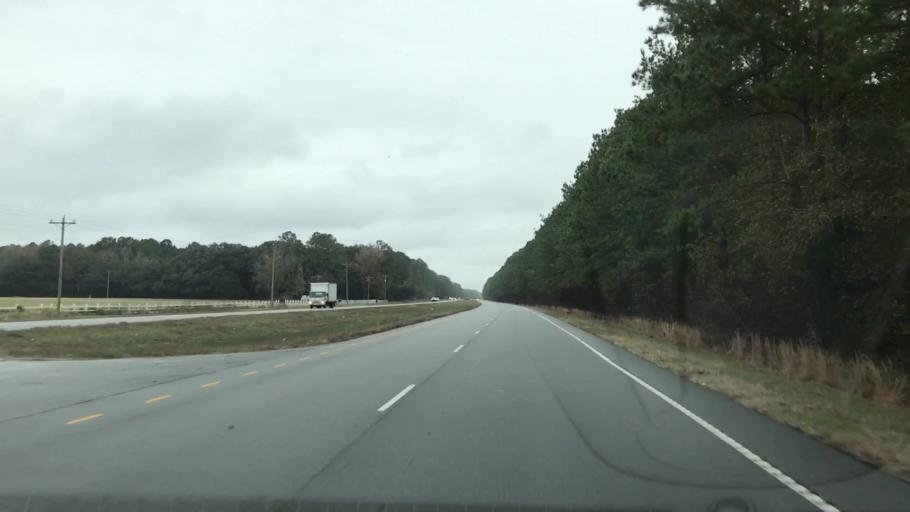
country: US
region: South Carolina
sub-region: Charleston County
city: Awendaw
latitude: 33.1230
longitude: -79.4511
